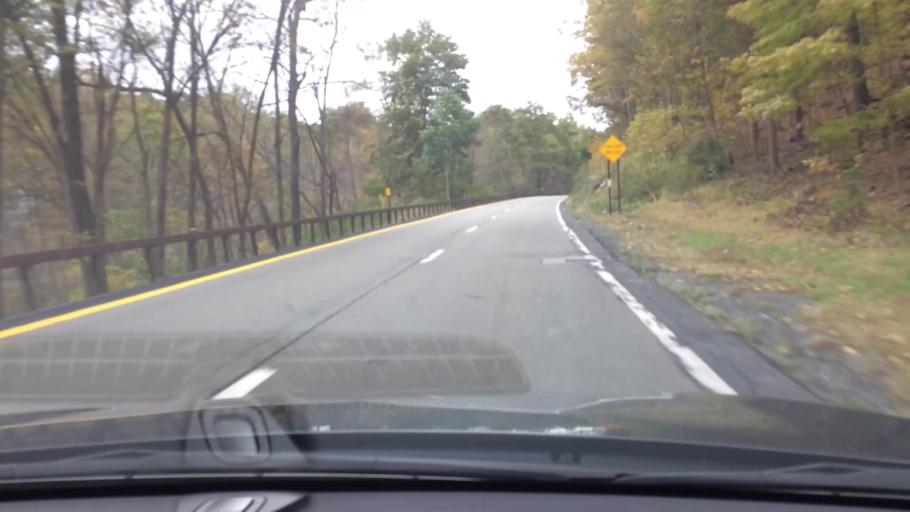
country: US
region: New York
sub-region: Dutchess County
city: Hillside Lake
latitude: 41.6169
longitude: -73.7638
